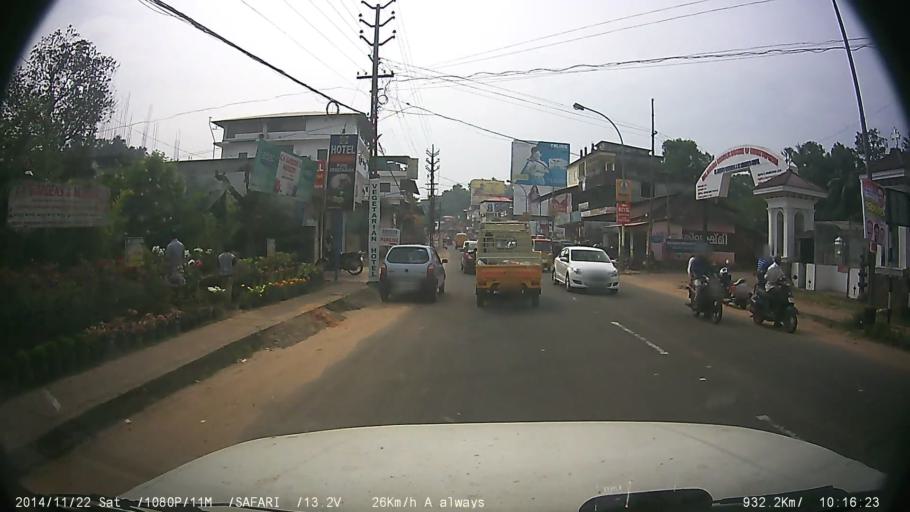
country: IN
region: Kerala
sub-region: Ernakulam
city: Muvattupula
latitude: 9.9962
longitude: 76.5723
